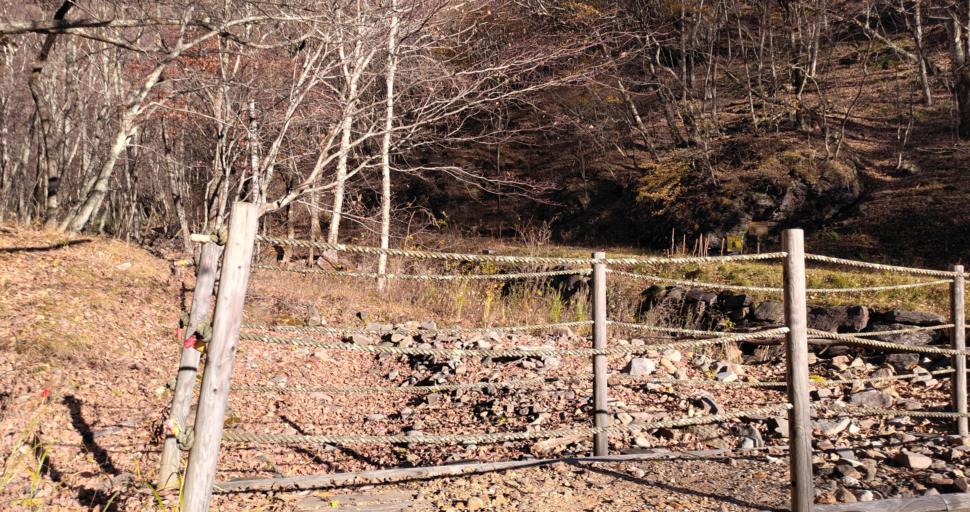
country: JP
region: Nagano
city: Komoro
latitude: 36.3985
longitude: 138.4443
